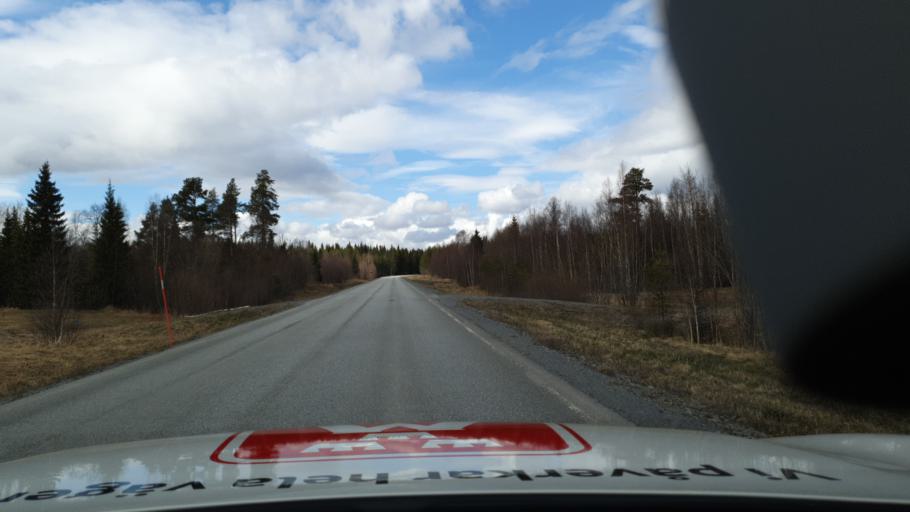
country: SE
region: Jaemtland
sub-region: Krokoms Kommun
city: Krokom
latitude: 63.2972
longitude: 14.4296
